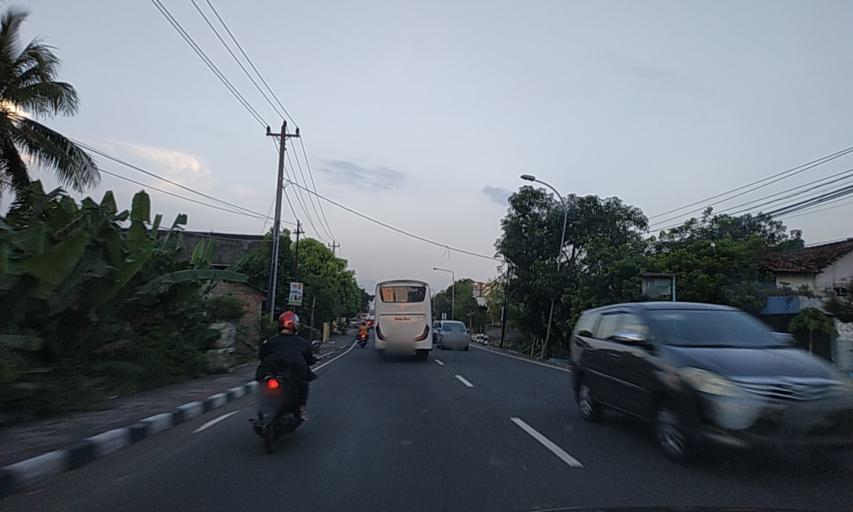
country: ID
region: Daerah Istimewa Yogyakarta
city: Srandakan
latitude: -7.8665
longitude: 110.1613
